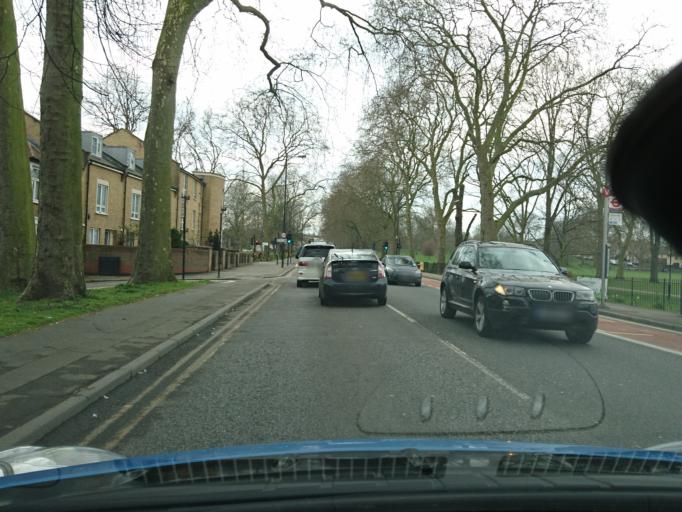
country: GB
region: England
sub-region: Greater London
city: Hackney
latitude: 51.5611
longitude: -0.0480
